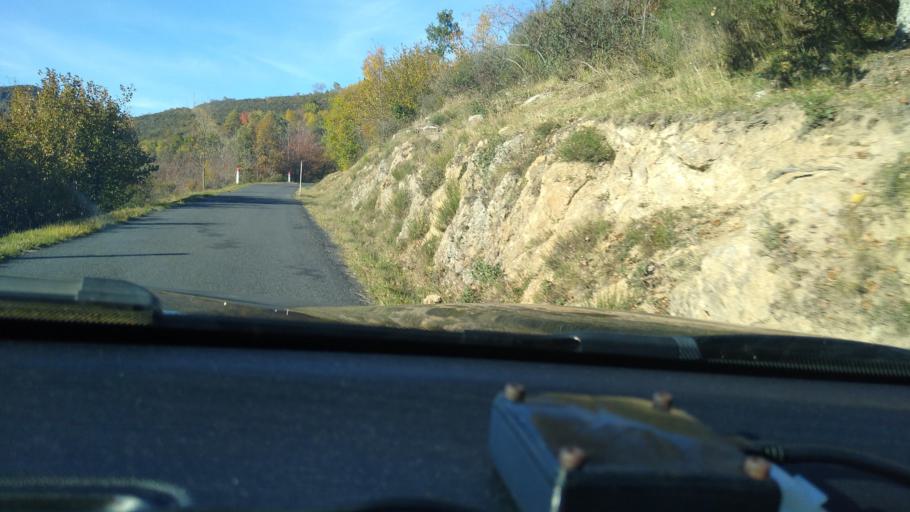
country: FR
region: Languedoc-Roussillon
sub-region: Departement de l'Aude
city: Quillan
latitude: 42.7264
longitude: 2.1195
